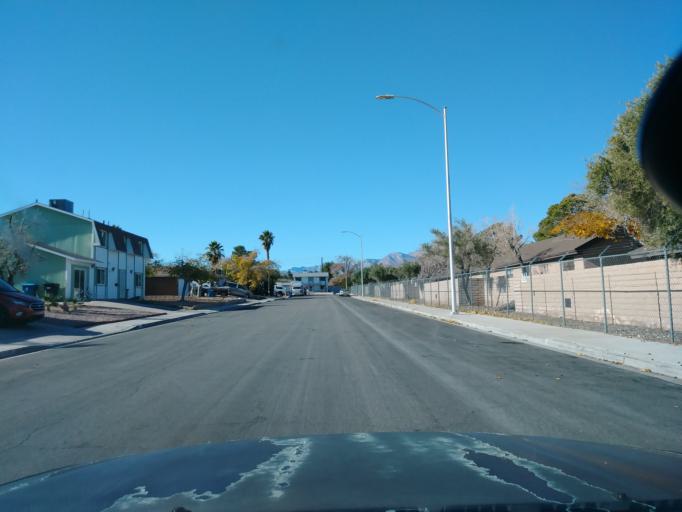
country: US
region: Nevada
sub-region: Clark County
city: Spring Valley
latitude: 36.1785
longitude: -115.2355
